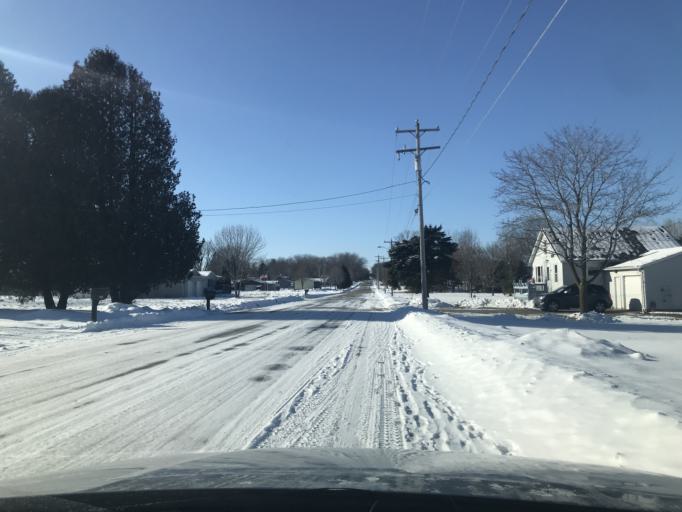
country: US
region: Wisconsin
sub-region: Oconto County
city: Oconto Falls
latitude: 44.9523
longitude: -88.0521
